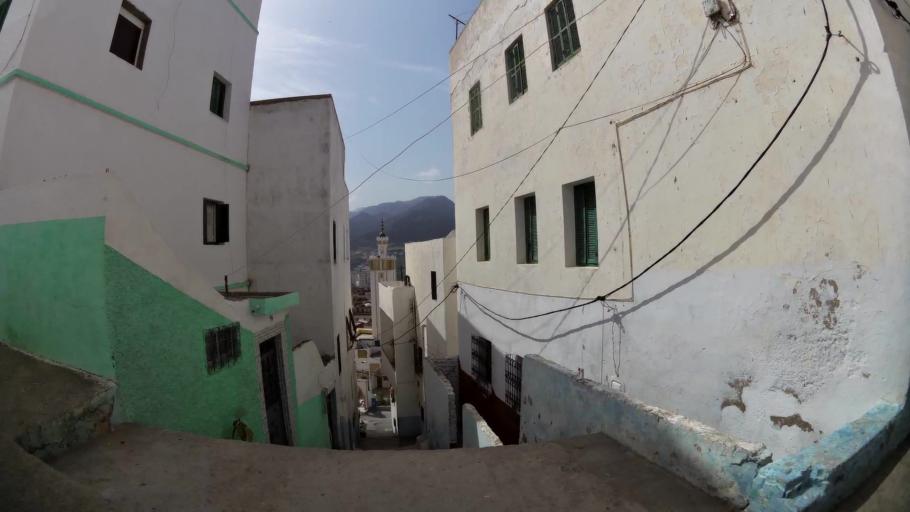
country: MA
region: Tanger-Tetouan
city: Tetouan
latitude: 35.5761
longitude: -5.3841
